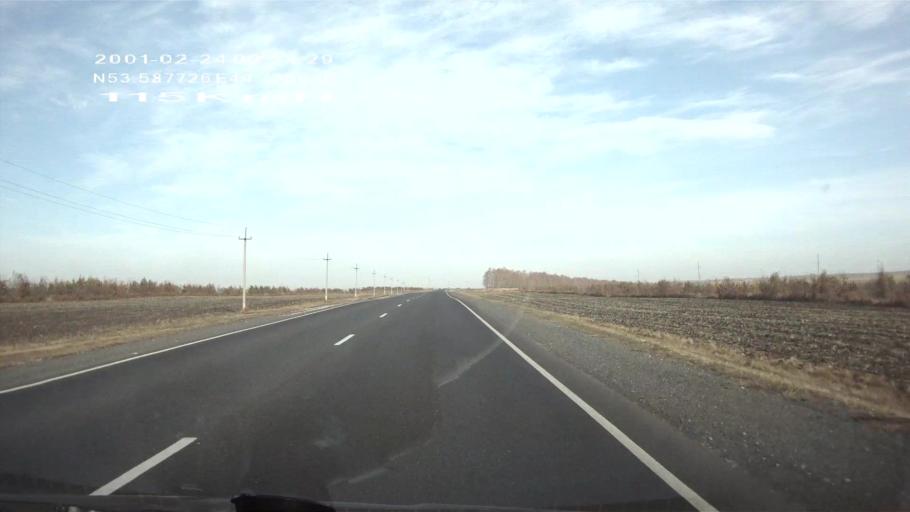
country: RU
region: Penza
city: Mokshan
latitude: 53.5873
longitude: 44.7269
